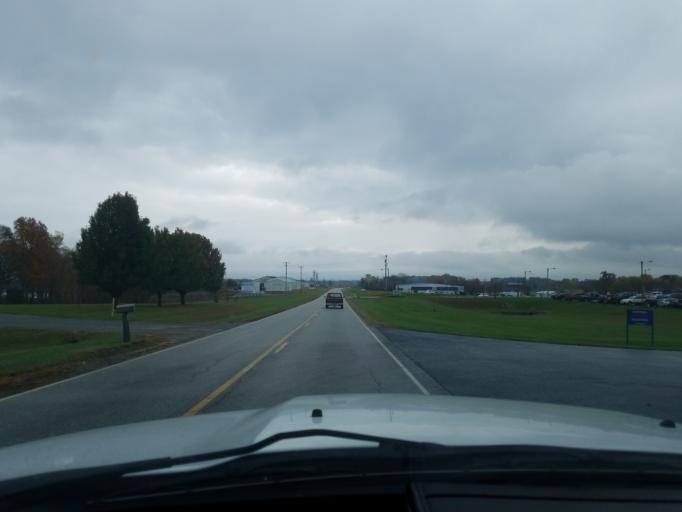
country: US
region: Kentucky
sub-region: Taylor County
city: Campbellsville
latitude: 37.3404
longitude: -85.3218
